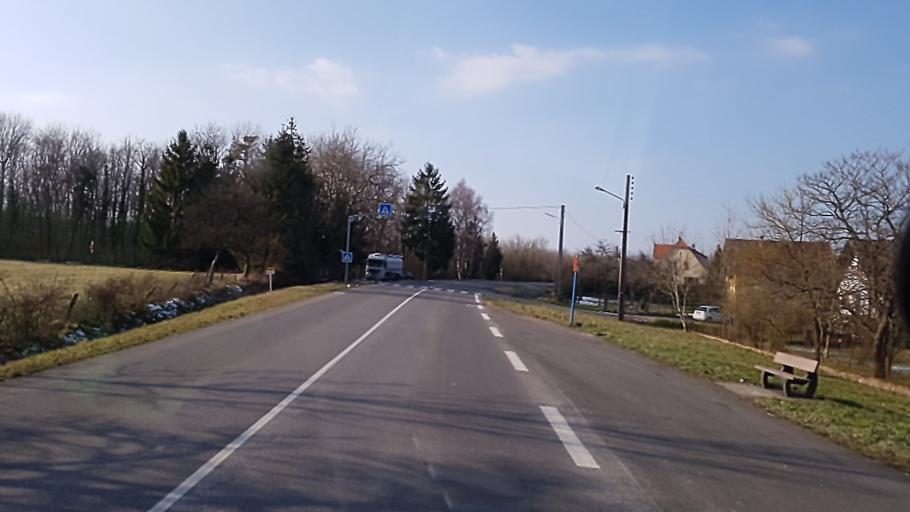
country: FR
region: Alsace
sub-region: Departement du Bas-Rhin
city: Drulingen
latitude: 48.8894
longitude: 7.1343
